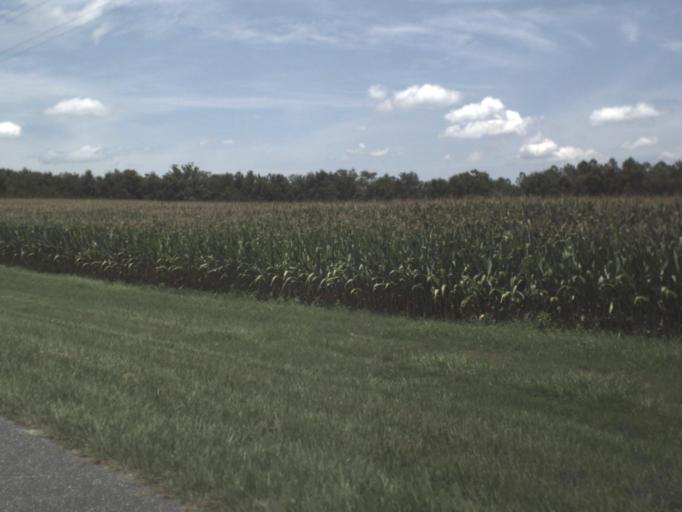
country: US
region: Florida
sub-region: Lafayette County
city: Mayo
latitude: 30.1853
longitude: -83.1300
